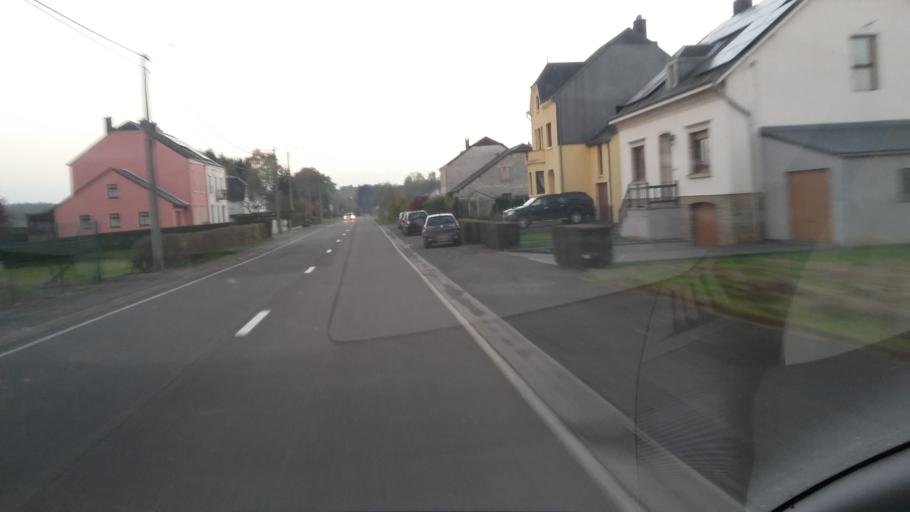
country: BE
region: Wallonia
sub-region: Province du Luxembourg
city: Etalle
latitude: 49.6688
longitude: 5.5987
